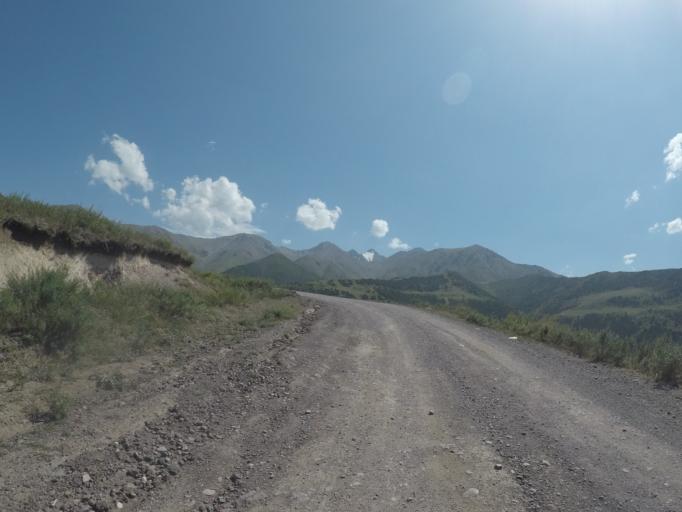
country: KG
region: Chuy
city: Bishkek
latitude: 42.6477
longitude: 74.5214
